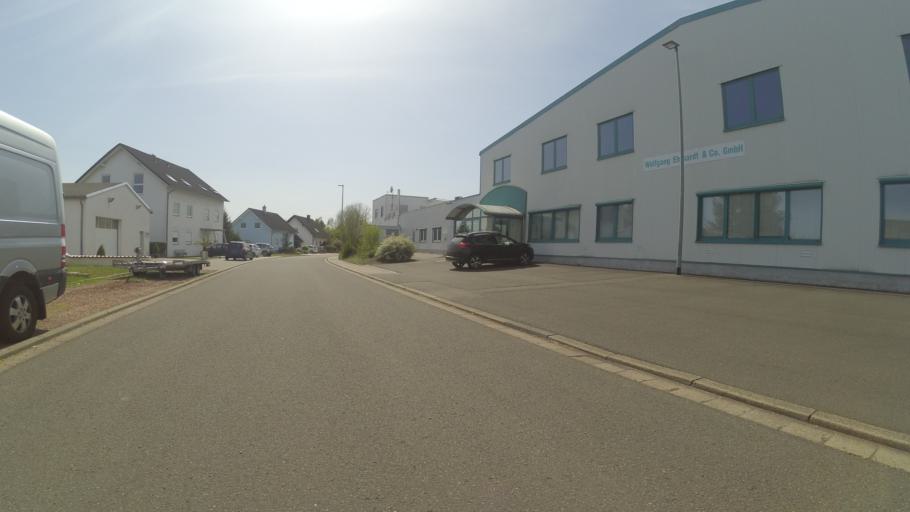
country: DE
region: Saarland
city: Homburg
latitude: 49.3476
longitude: 7.3466
